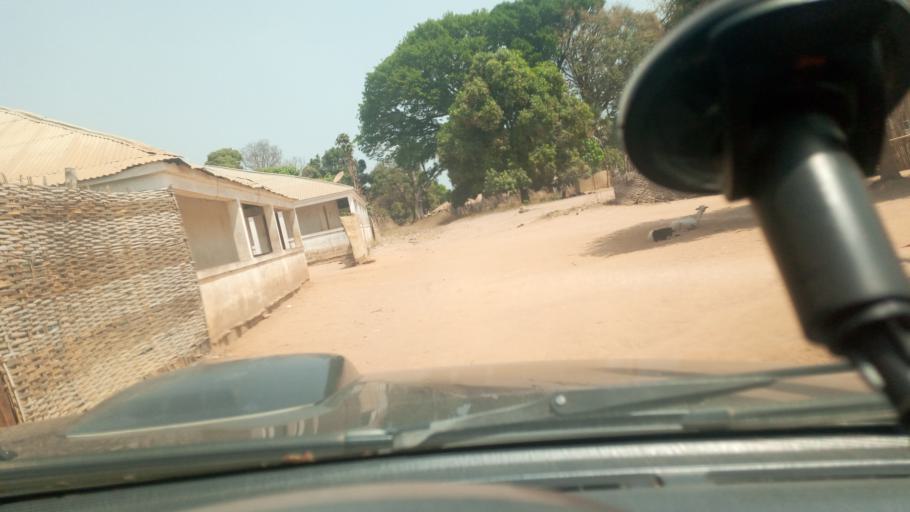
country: SN
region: Sedhiou
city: Sedhiou
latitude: 12.4418
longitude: -15.6160
